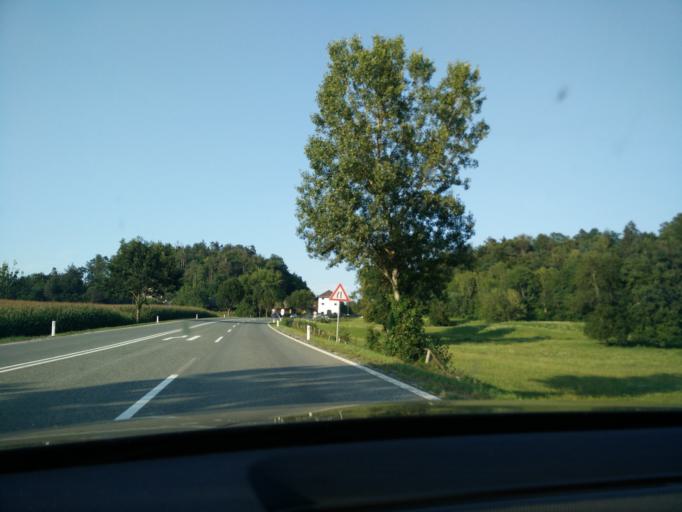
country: AT
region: Carinthia
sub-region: Politischer Bezirk Klagenfurt Land
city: Kottmannsdorf
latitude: 46.5479
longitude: 14.2579
